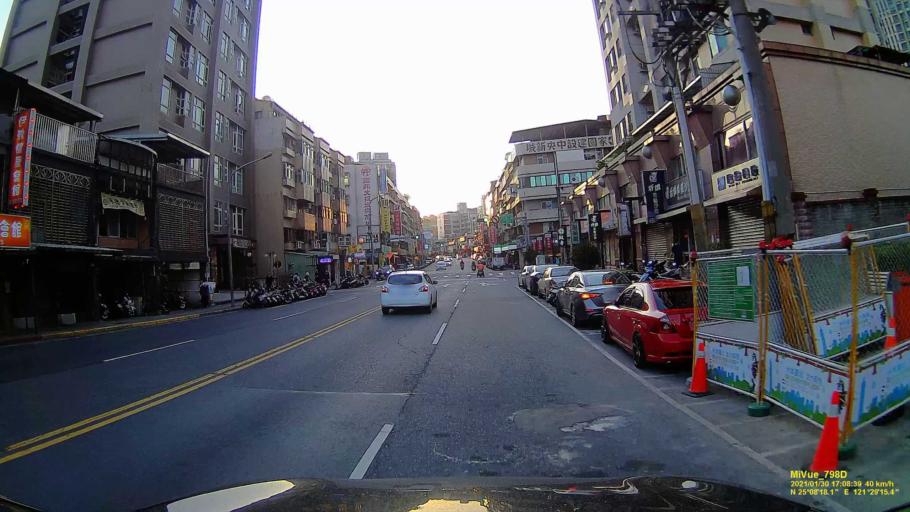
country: TW
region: Taipei
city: Taipei
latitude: 25.1383
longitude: 121.4874
